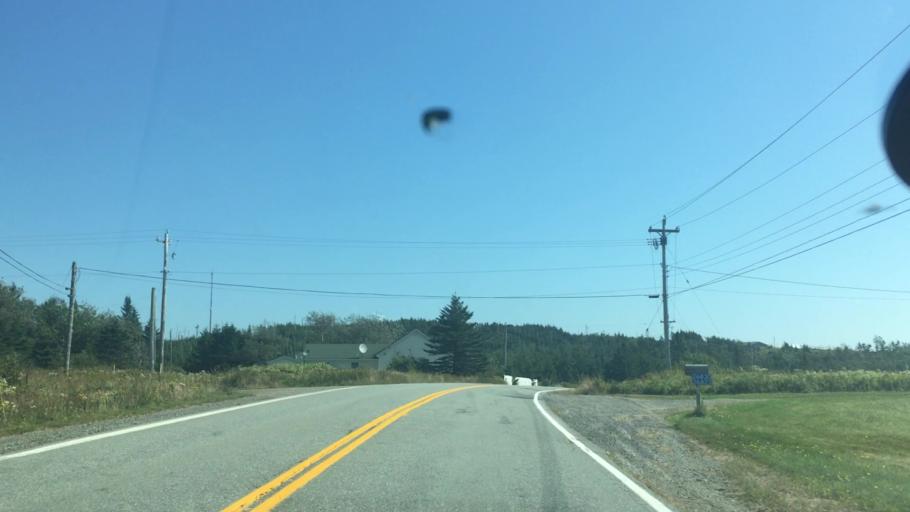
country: CA
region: Nova Scotia
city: New Glasgow
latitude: 44.9174
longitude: -62.3246
